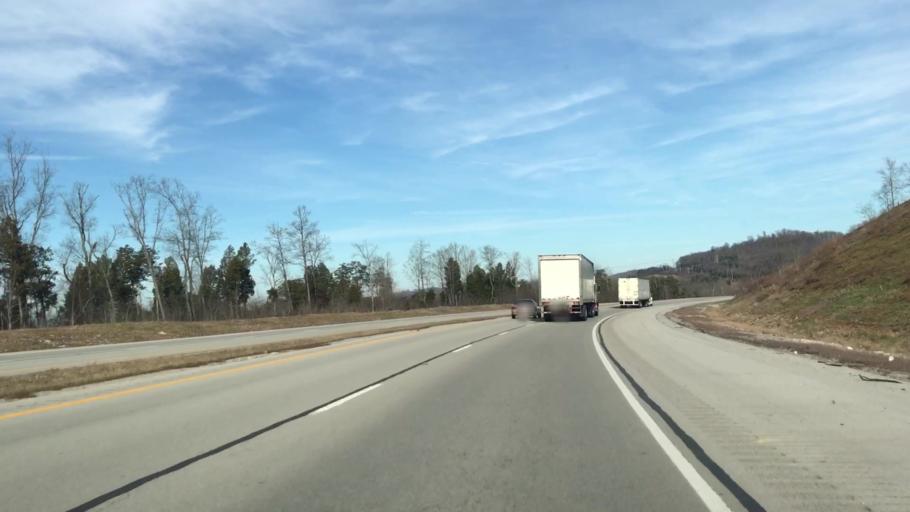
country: US
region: Kentucky
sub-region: Pulaski County
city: Somerset
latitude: 37.0152
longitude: -84.6002
